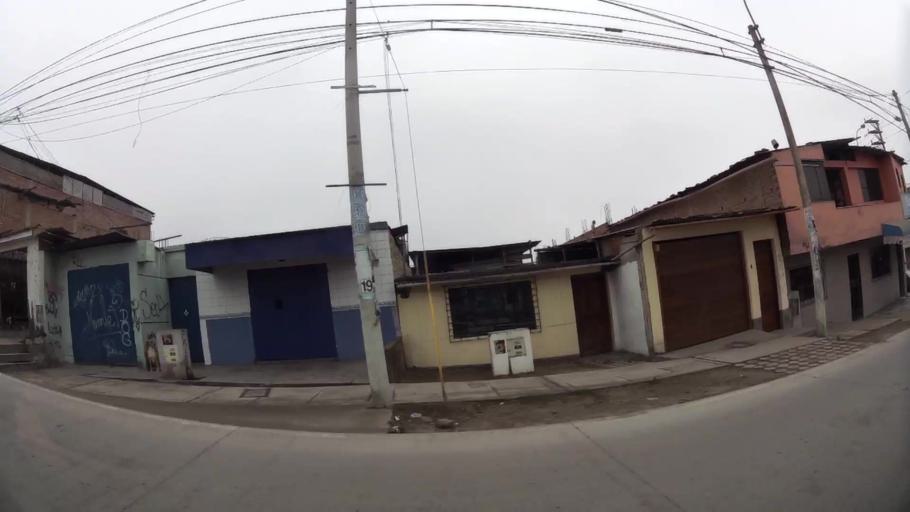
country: PE
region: Lima
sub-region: Lima
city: Surco
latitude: -12.1906
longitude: -76.9308
